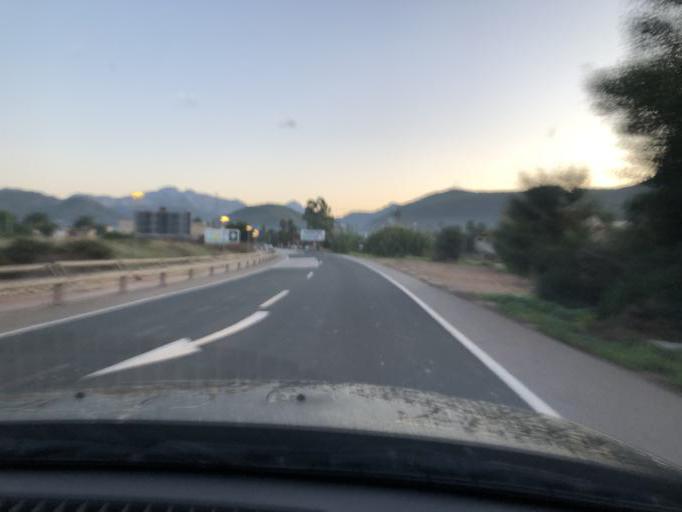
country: ES
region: Balearic Islands
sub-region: Illes Balears
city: Camp de Mar
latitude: 39.5476
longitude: 2.3944
